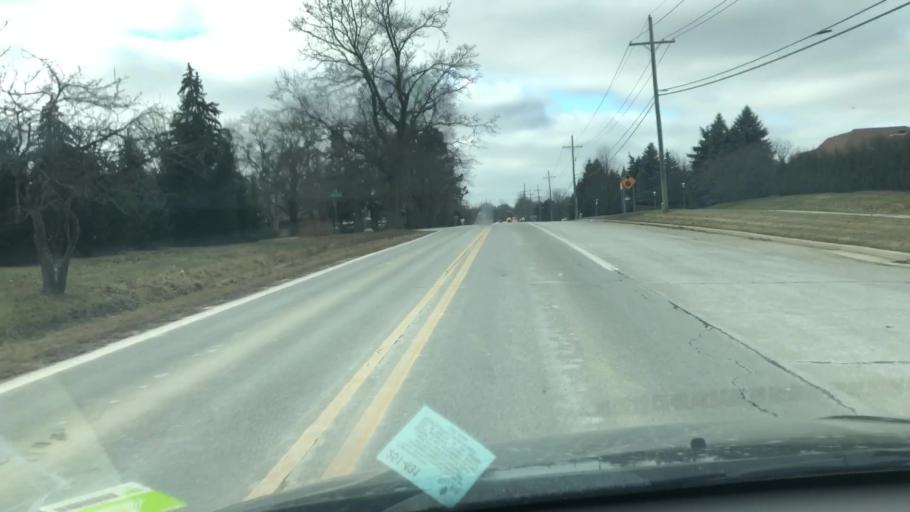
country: US
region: Michigan
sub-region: Macomb County
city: Romeo
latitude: 42.7430
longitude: -83.0331
